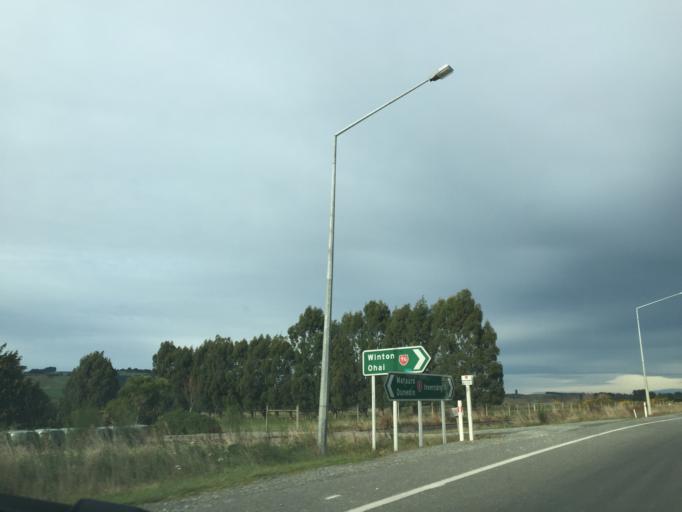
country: NZ
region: Southland
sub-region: Gore District
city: Gore
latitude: -46.2038
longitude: 168.8531
